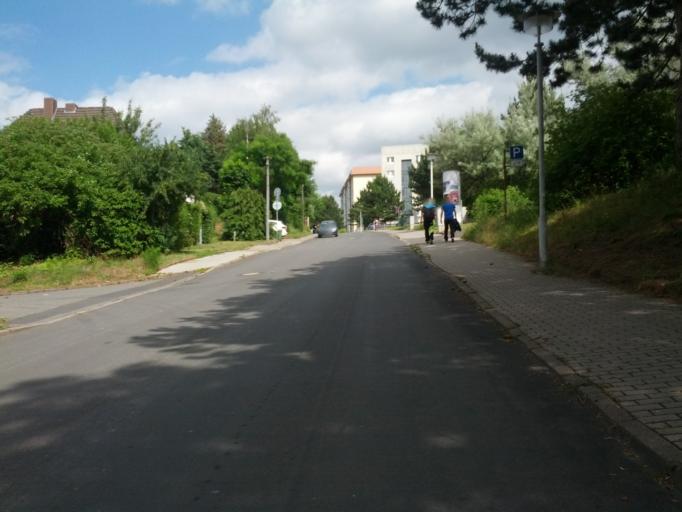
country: DE
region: Thuringia
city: Eisenach
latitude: 50.9786
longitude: 10.3449
